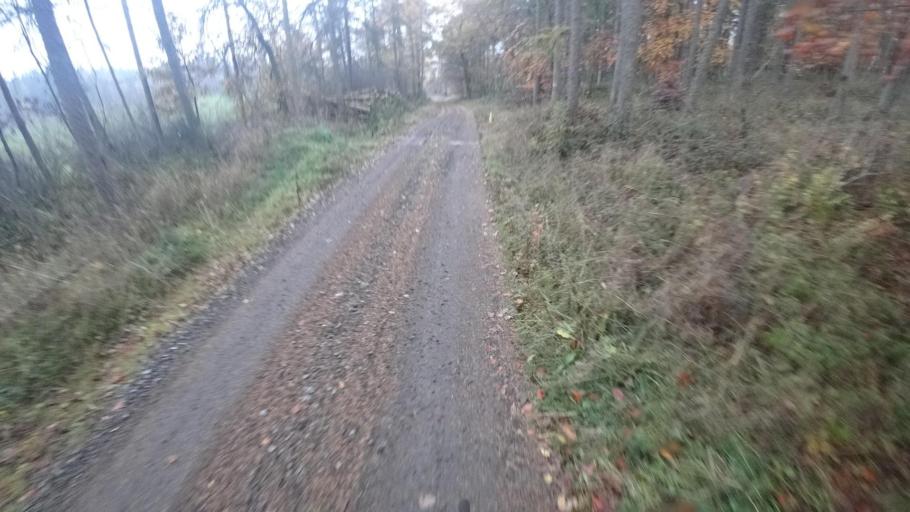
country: DE
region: Rheinland-Pfalz
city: Rech
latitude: 50.5011
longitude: 7.0577
